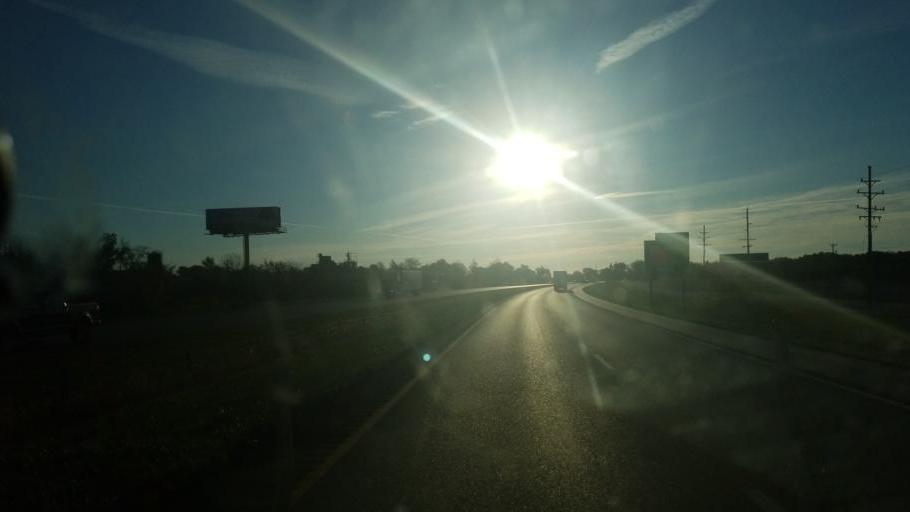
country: US
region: Missouri
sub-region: Montgomery County
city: Montgomery City
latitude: 38.8809
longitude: -91.3924
